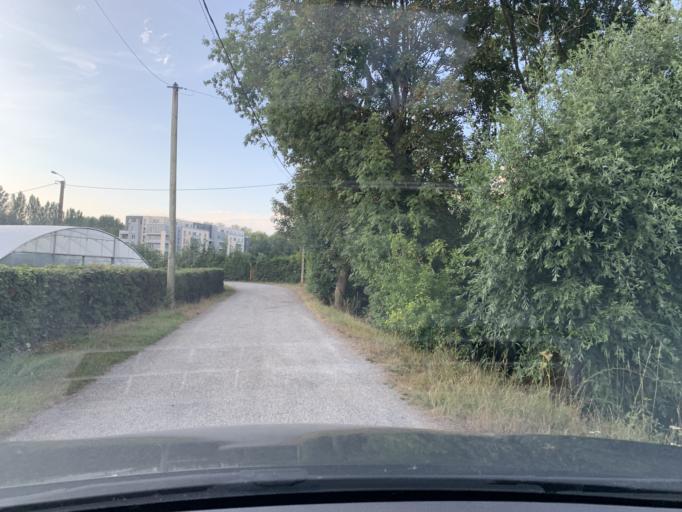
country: FR
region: Nord-Pas-de-Calais
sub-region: Departement du Nord
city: Cambrai
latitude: 50.1710
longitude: 3.2219
